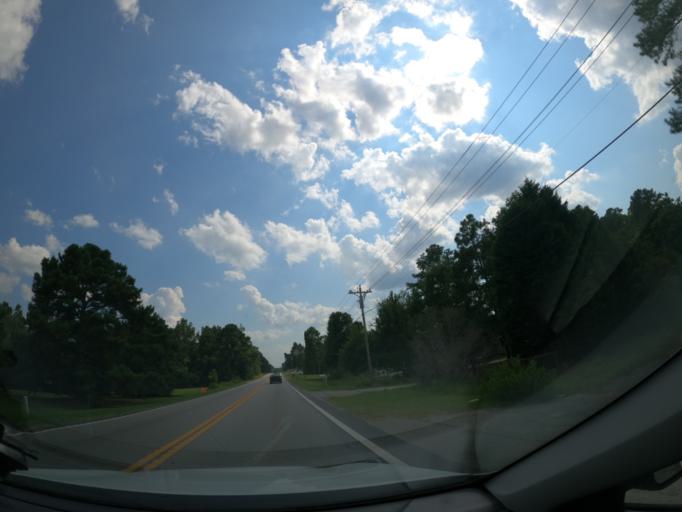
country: US
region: South Carolina
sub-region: Lexington County
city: Red Bank
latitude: 33.8496
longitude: -81.2073
